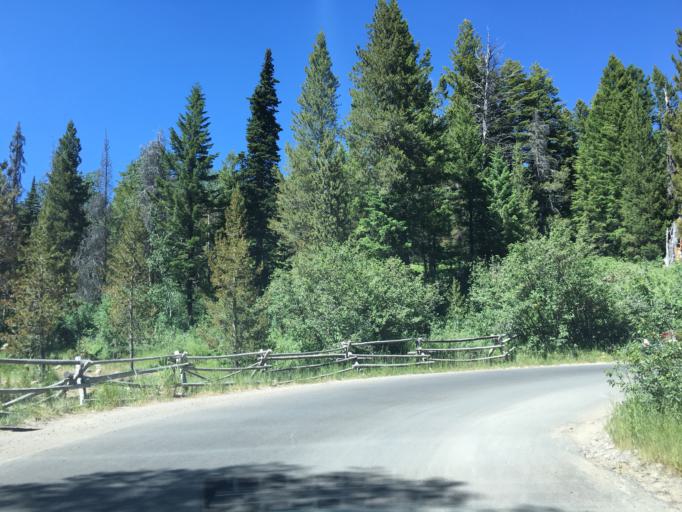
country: US
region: Wyoming
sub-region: Teton County
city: Moose Wilson Road
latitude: 43.6231
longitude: -110.7869
